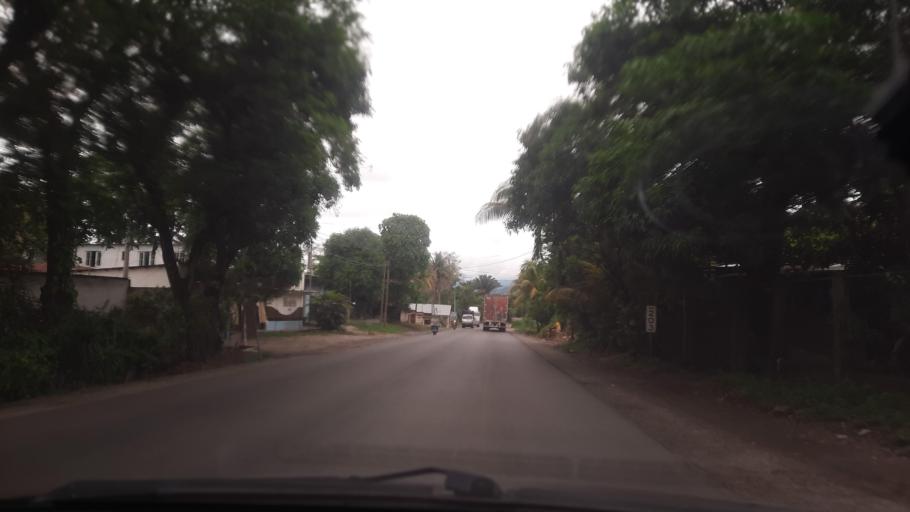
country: GT
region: Izabal
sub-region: Municipio de Los Amates
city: Los Amates
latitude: 15.2722
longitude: -89.0806
